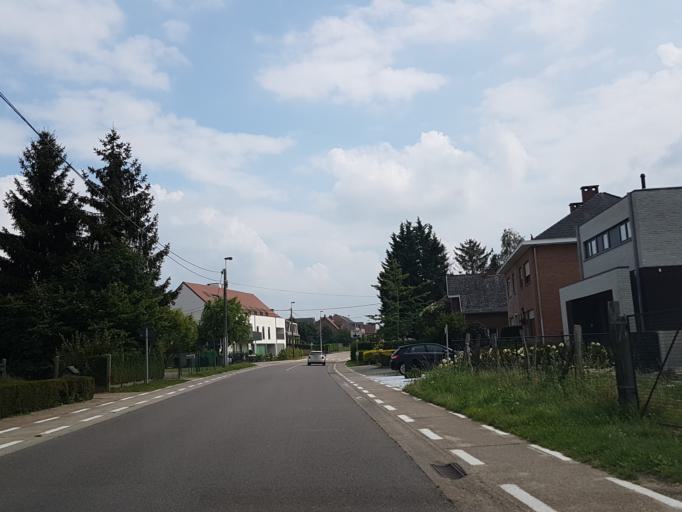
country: BE
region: Flanders
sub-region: Provincie Vlaams-Brabant
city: Kortenberg
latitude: 50.8824
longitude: 4.5832
